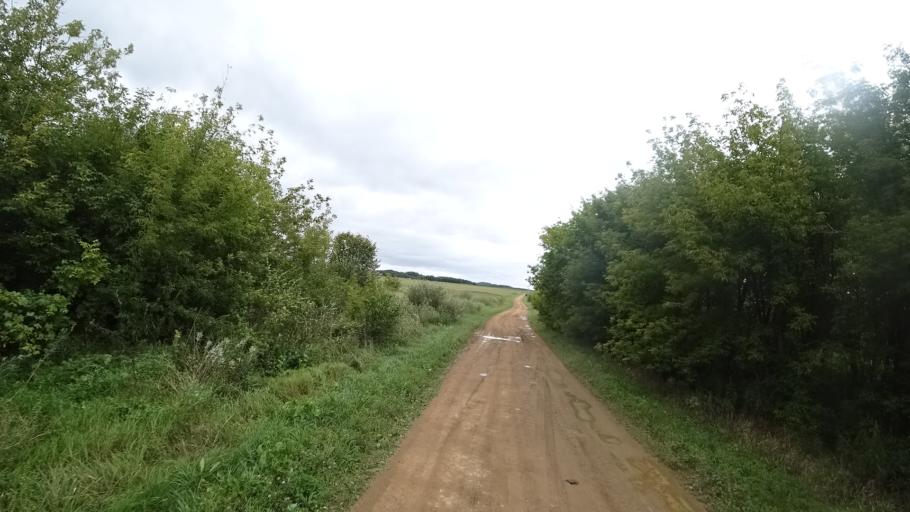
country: RU
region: Primorskiy
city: Chernigovka
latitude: 44.4333
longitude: 132.5922
